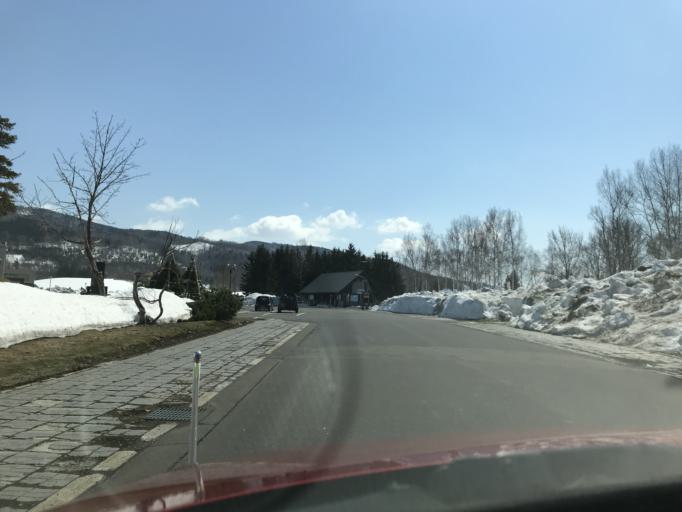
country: JP
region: Hokkaido
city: Nayoro
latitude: 44.5582
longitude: 142.3229
